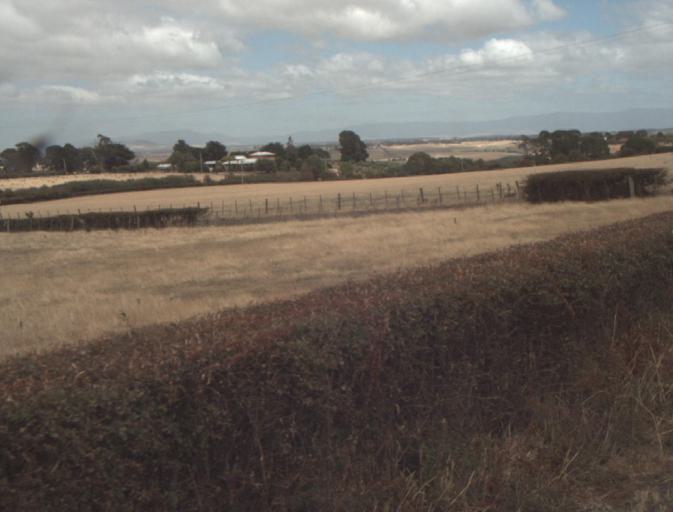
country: AU
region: Tasmania
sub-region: Northern Midlands
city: Evandale
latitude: -41.5211
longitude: 147.2831
